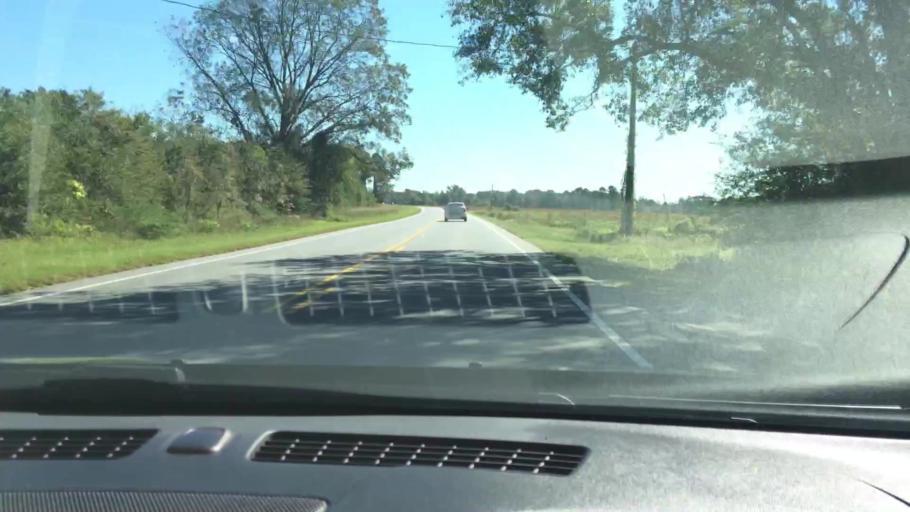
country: US
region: North Carolina
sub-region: Pitt County
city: Grifton
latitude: 35.3533
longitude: -77.3355
